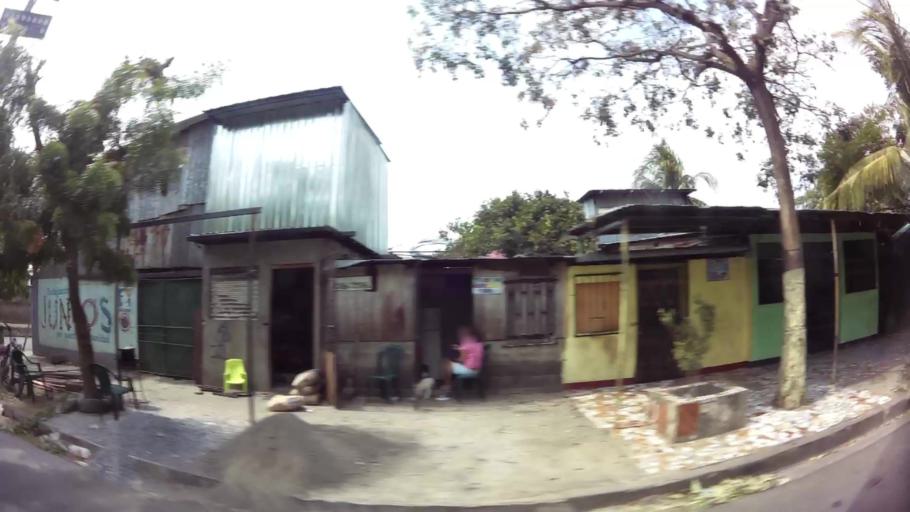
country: NI
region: Managua
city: Managua
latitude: 12.1498
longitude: -86.2678
